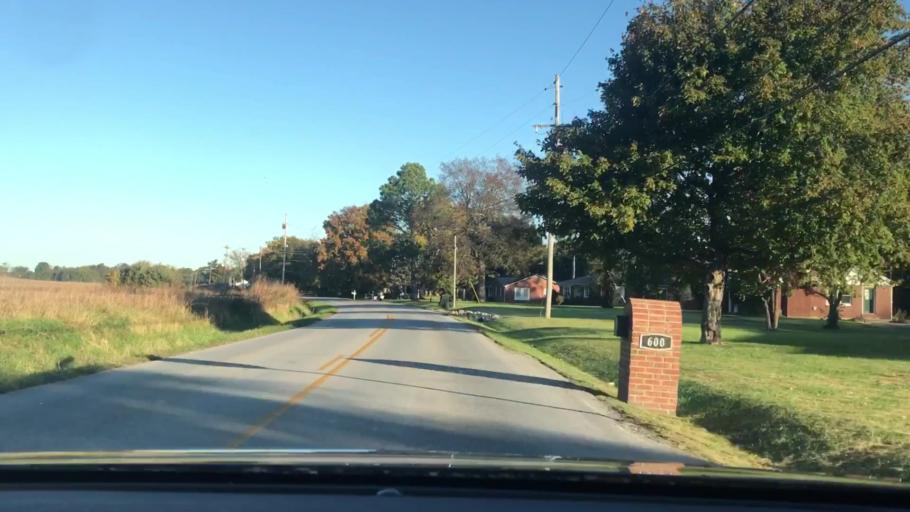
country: US
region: Kentucky
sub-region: Simpson County
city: Franklin
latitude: 36.7378
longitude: -86.5846
